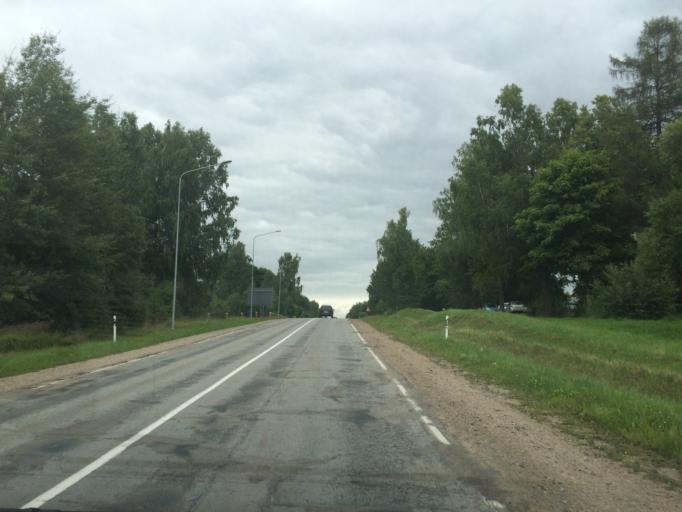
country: LV
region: Rezekne
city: Rezekne
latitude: 56.5468
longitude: 27.3555
